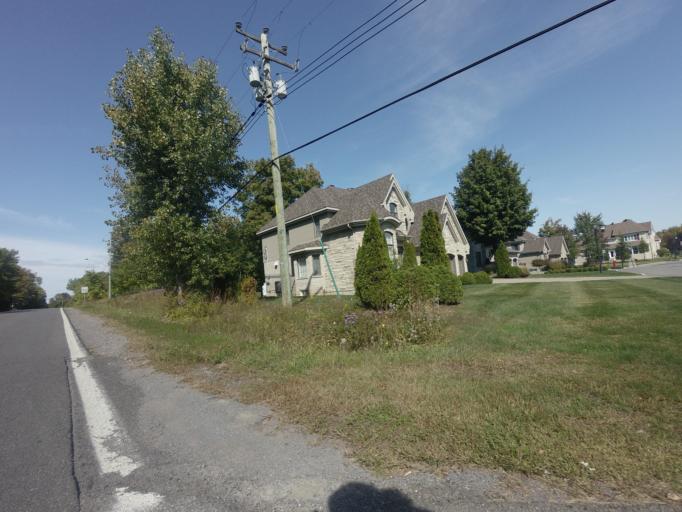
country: CA
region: Quebec
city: Dollard-Des Ormeaux
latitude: 45.5128
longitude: -73.8612
